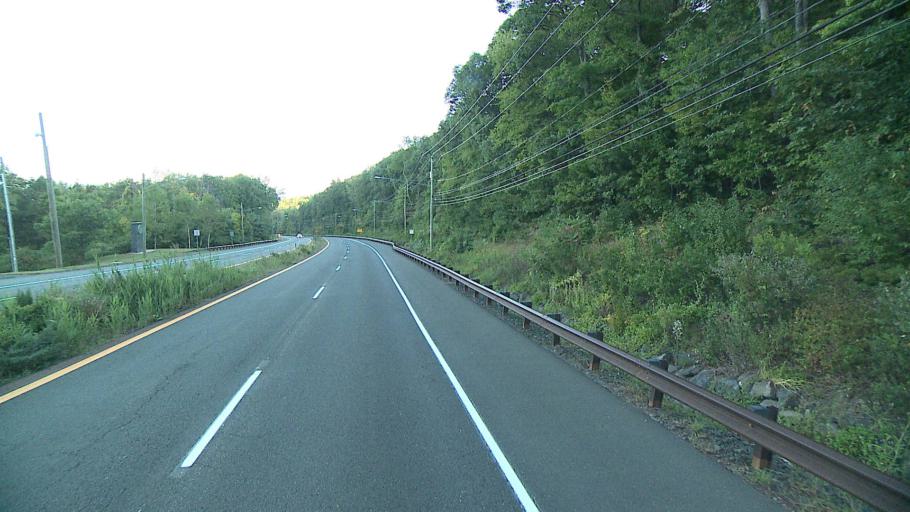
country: US
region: Connecticut
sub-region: Hartford County
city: Weatogue
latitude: 41.8010
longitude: -72.8034
